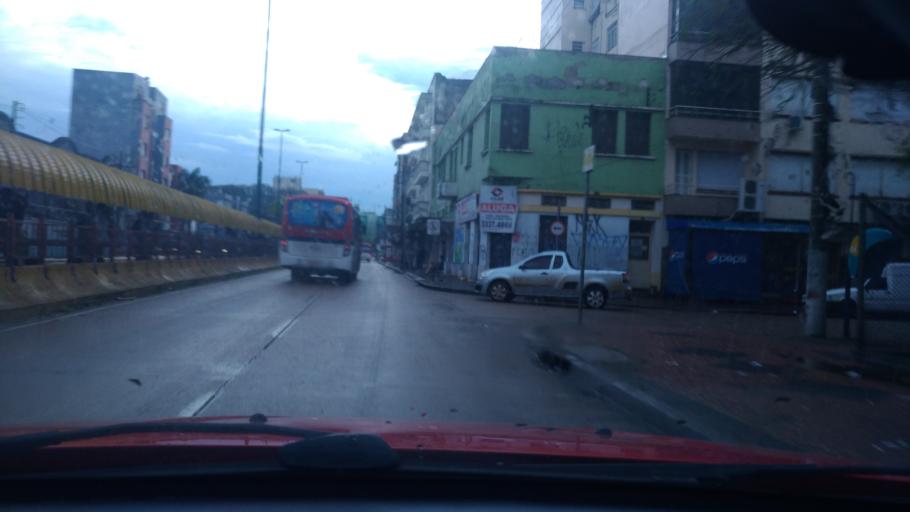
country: BR
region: Rio Grande do Sul
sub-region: Porto Alegre
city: Porto Alegre
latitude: -30.0204
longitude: -51.2106
